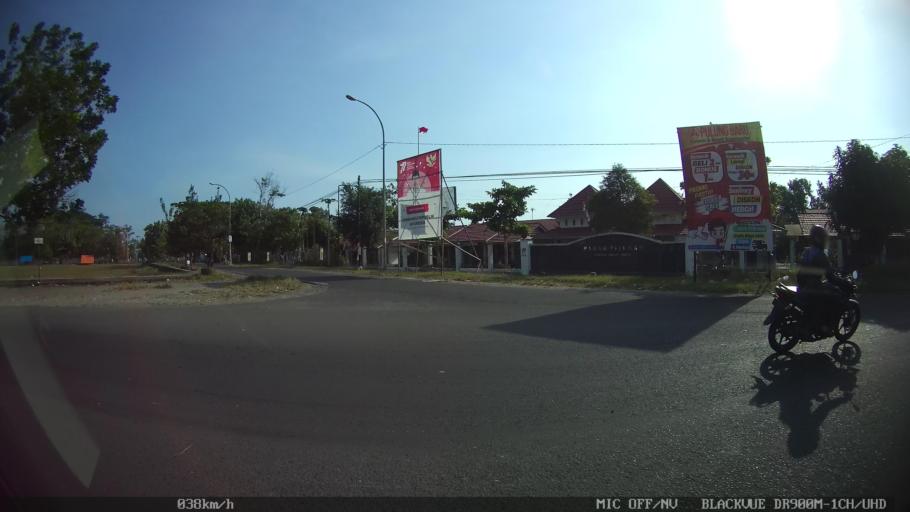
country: ID
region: Daerah Istimewa Yogyakarta
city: Pandak
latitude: -7.8998
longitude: 110.2978
